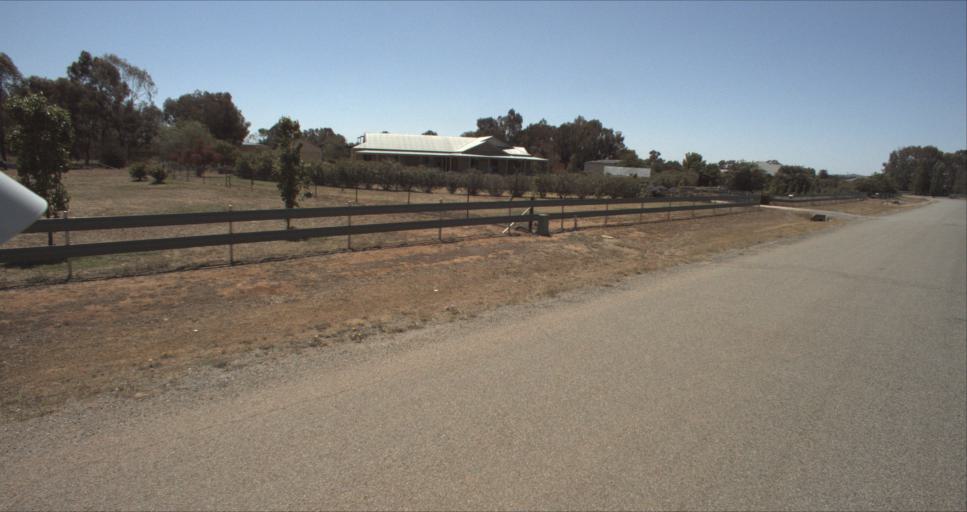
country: AU
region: New South Wales
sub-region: Leeton
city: Leeton
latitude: -34.5303
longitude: 146.3967
